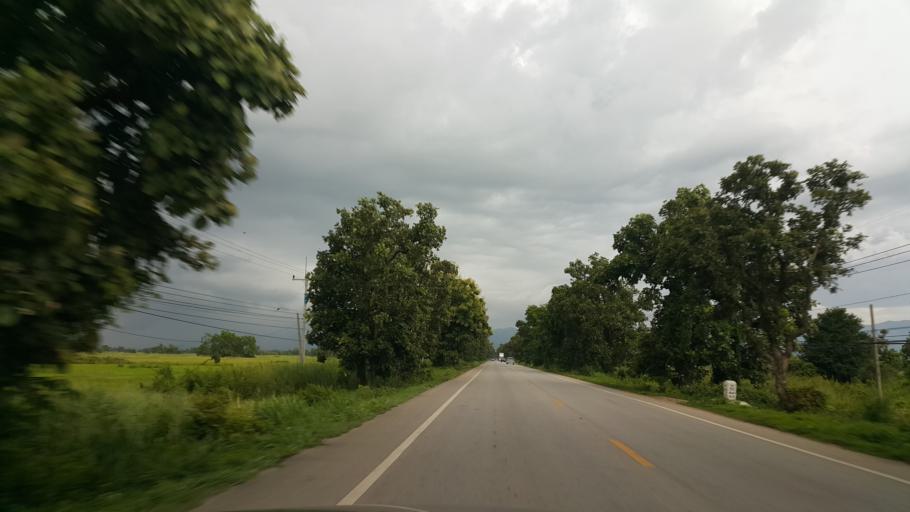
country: TH
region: Phayao
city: Dok Kham Tai
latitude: 19.1856
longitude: 100.0183
